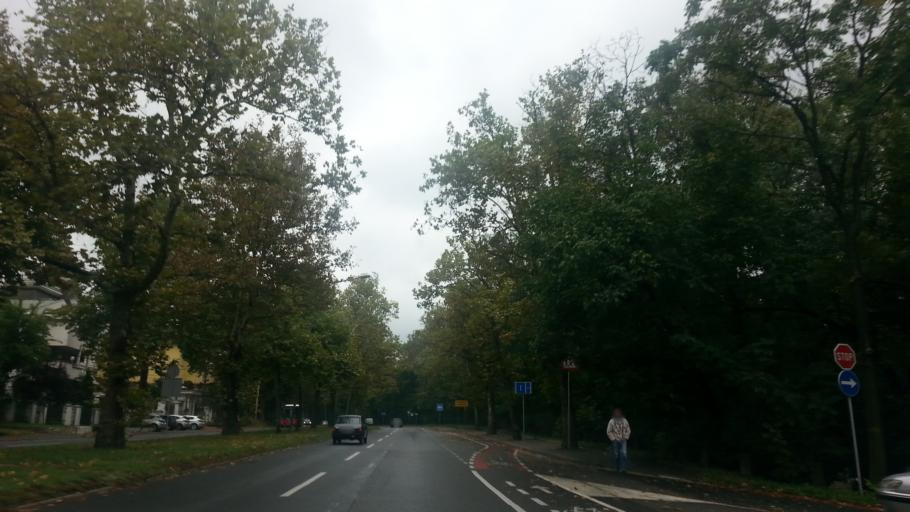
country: RS
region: Central Serbia
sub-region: Belgrade
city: Vozdovac
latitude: 44.7753
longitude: 20.4731
